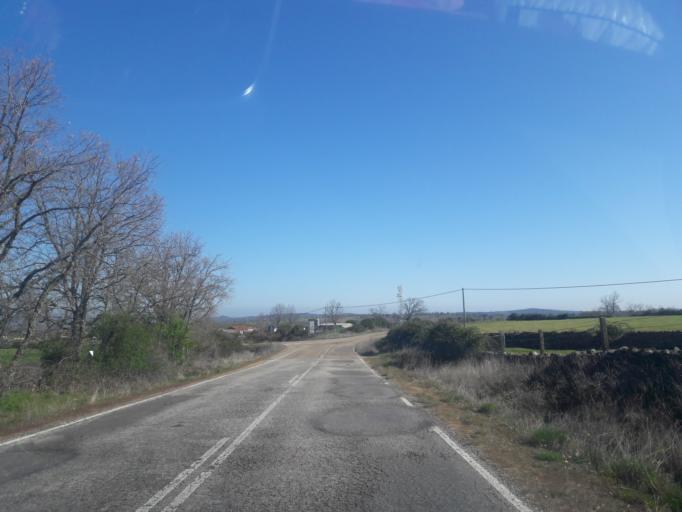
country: ES
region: Castille and Leon
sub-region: Provincia de Salamanca
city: Cabeza del Caballo
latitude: 41.1594
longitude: -6.5518
